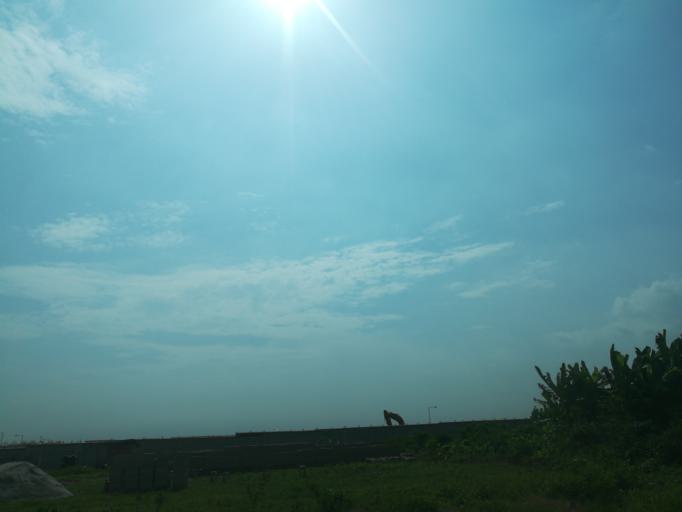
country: NG
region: Lagos
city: Ikorodu
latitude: 6.6371
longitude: 3.6700
